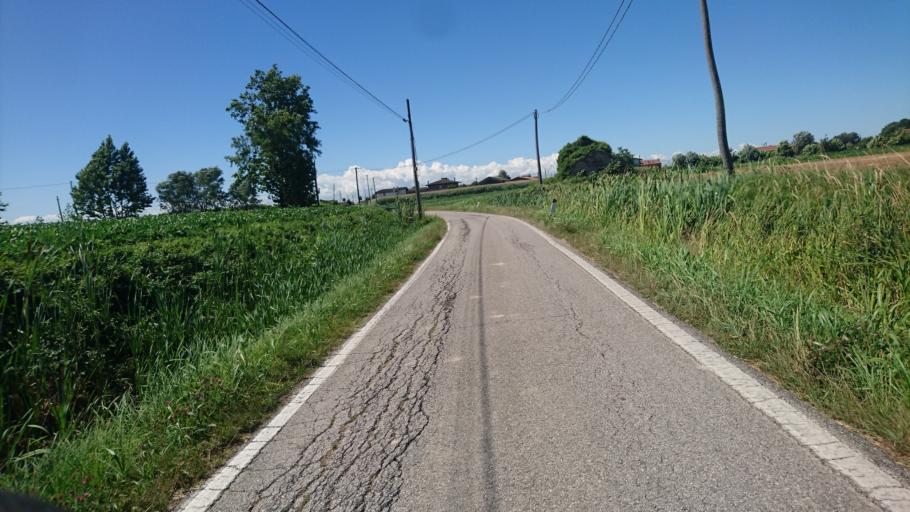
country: IT
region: Veneto
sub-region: Provincia di Padova
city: Campagnola
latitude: 45.2663
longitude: 12.0153
